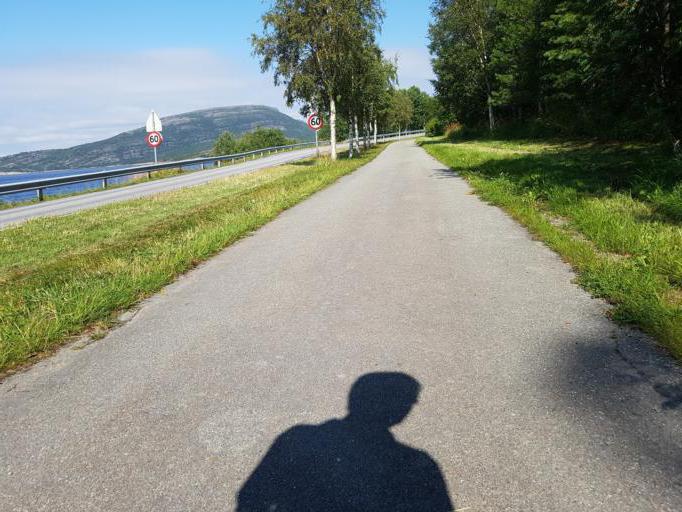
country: NO
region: Sor-Trondelag
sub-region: Agdenes
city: Lensvik
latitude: 63.6336
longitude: 9.8305
